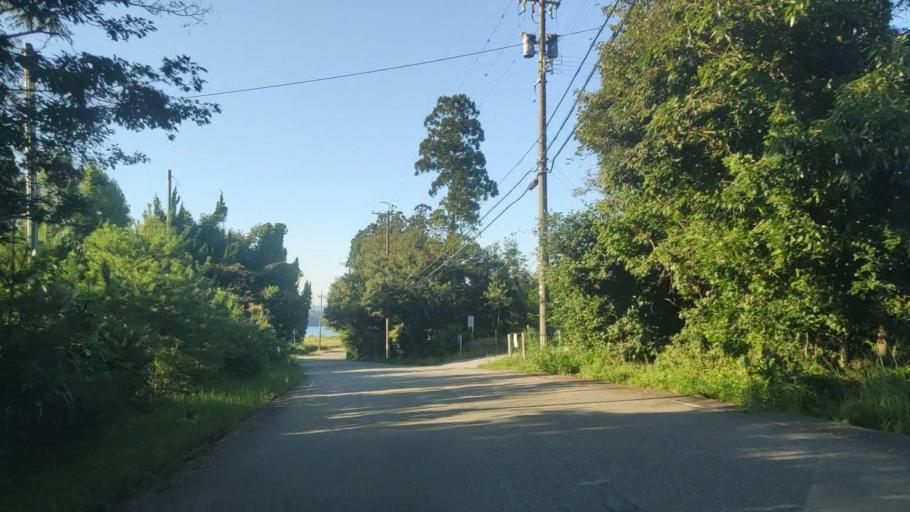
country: JP
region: Ishikawa
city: Nanao
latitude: 37.1291
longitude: 136.9317
